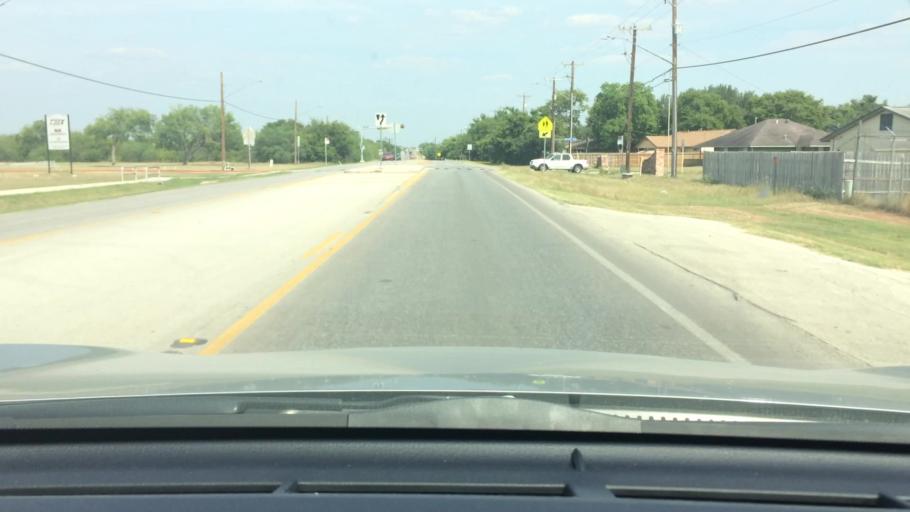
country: US
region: Texas
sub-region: Bexar County
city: China Grove
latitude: 29.3282
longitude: -98.4384
